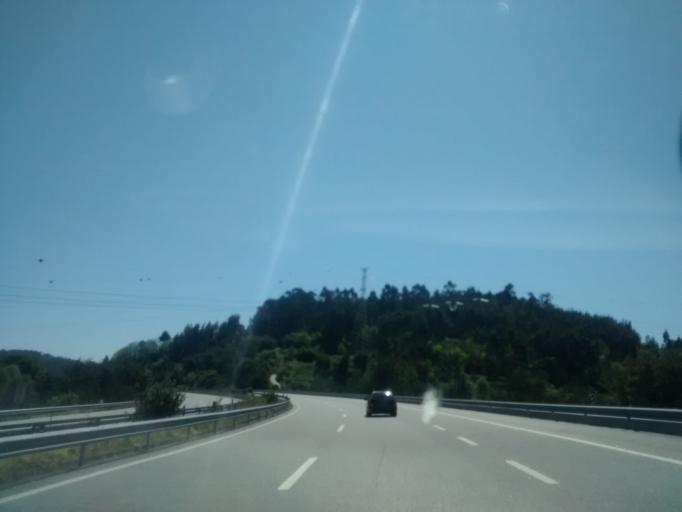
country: PT
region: Braga
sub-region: Guimaraes
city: Candoso
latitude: 41.4232
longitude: -8.3305
